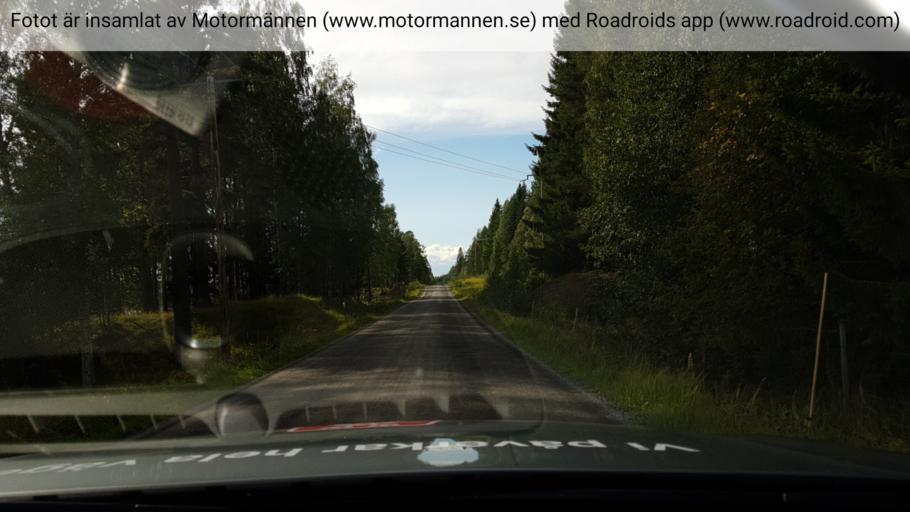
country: SE
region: Jaemtland
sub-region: Braecke Kommun
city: Braecke
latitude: 63.1956
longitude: 15.4975
